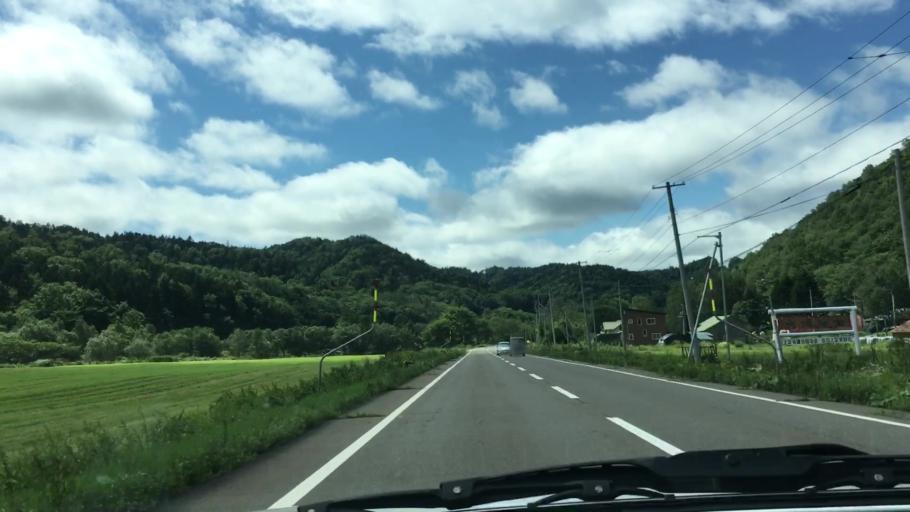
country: JP
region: Hokkaido
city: Kitami
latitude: 43.3638
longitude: 143.8559
